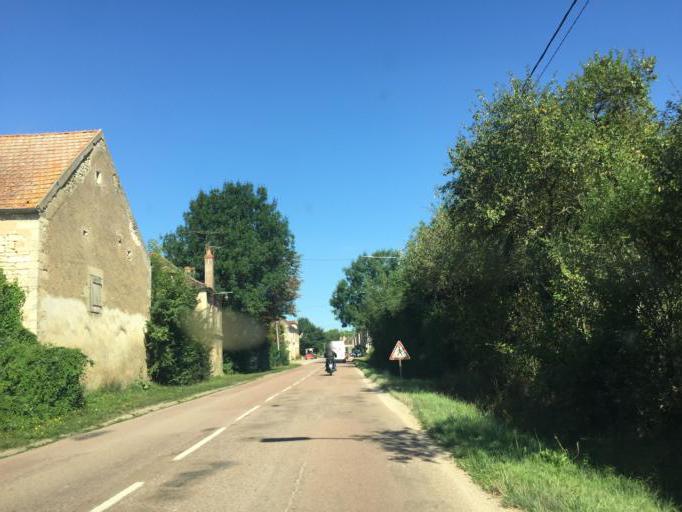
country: FR
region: Bourgogne
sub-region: Departement de la Nievre
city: Clamecy
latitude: 47.4526
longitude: 3.4721
